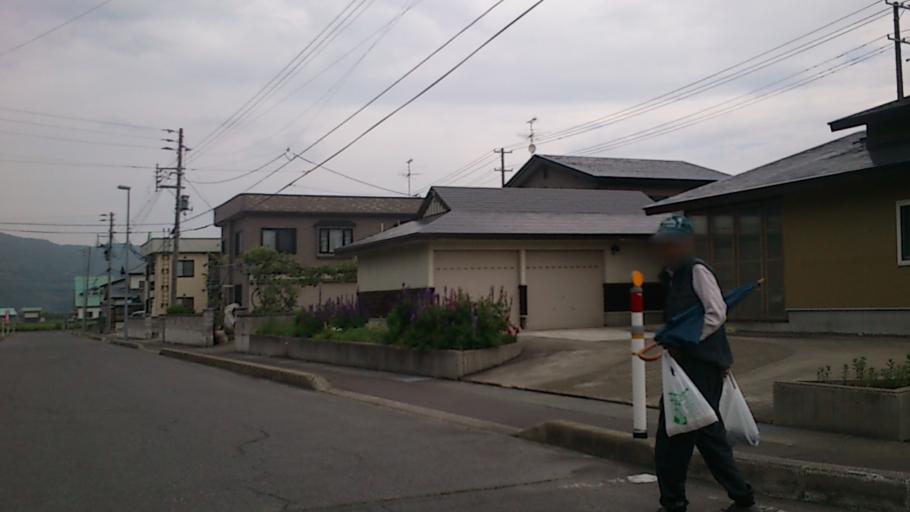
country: JP
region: Aomori
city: Hirosaki
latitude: 40.5787
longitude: 140.2997
